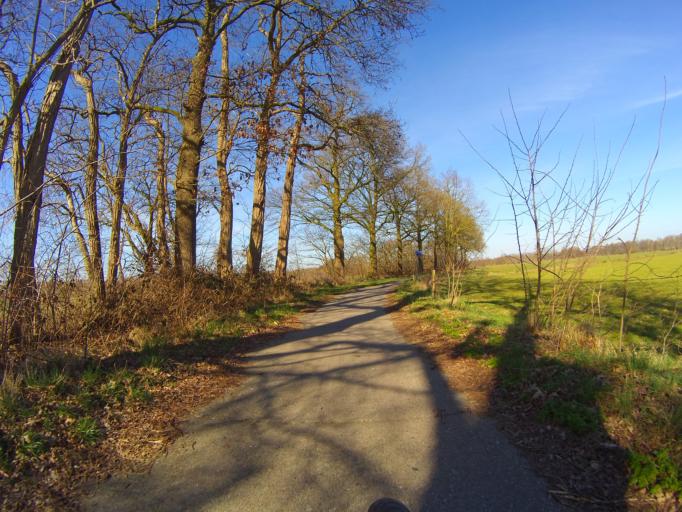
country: NL
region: Utrecht
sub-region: Gemeente Utrechtse Heuvelrug
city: Overberg
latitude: 52.0626
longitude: 5.4924
